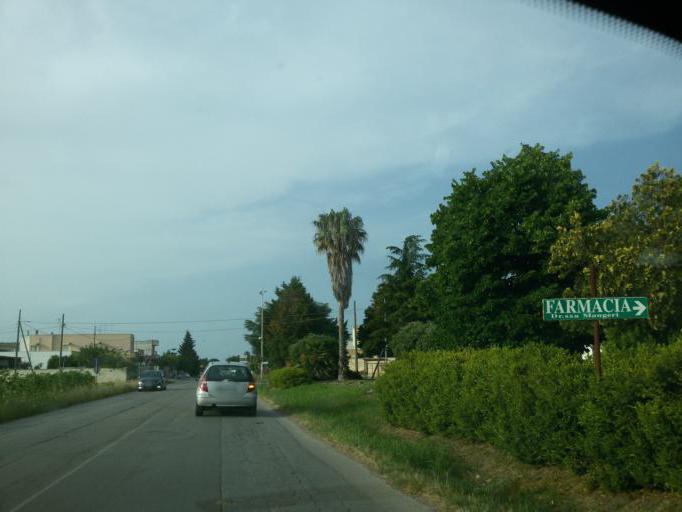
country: IT
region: Apulia
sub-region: Provincia di Brindisi
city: San Pietro Vernotico
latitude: 40.4941
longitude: 17.9906
